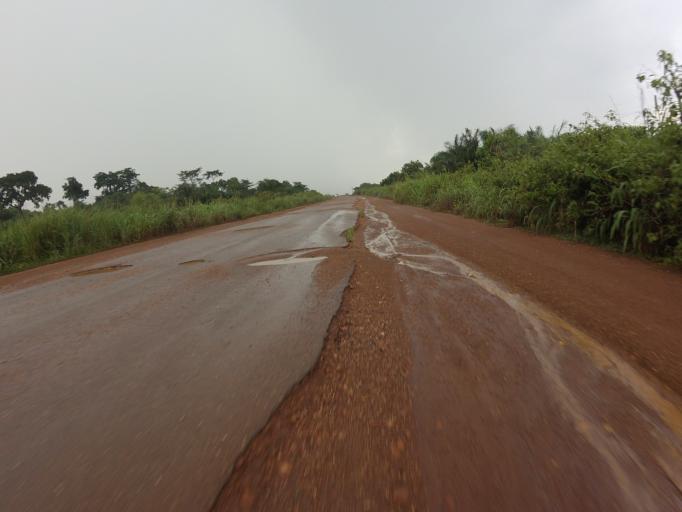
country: GH
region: Volta
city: Hohoe
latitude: 7.0616
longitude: 0.4315
